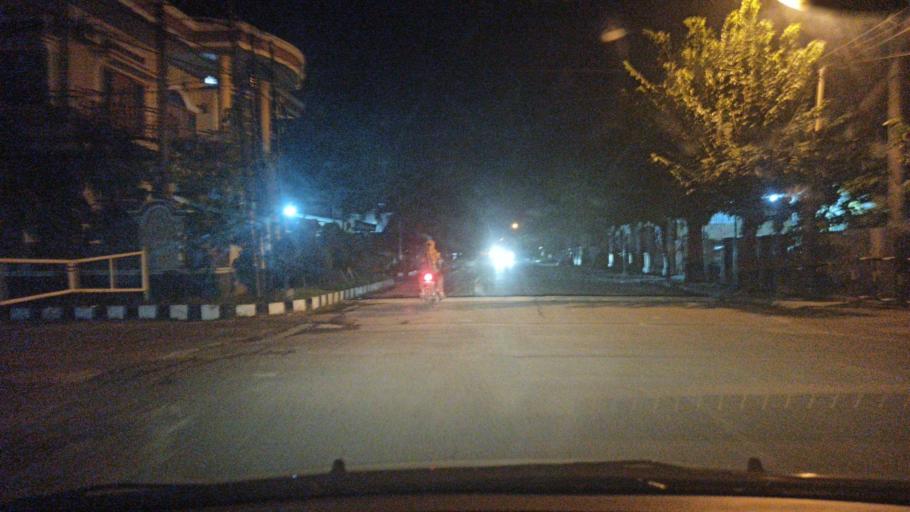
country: ID
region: South Sumatra
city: Plaju
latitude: -3.0081
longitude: 104.7158
